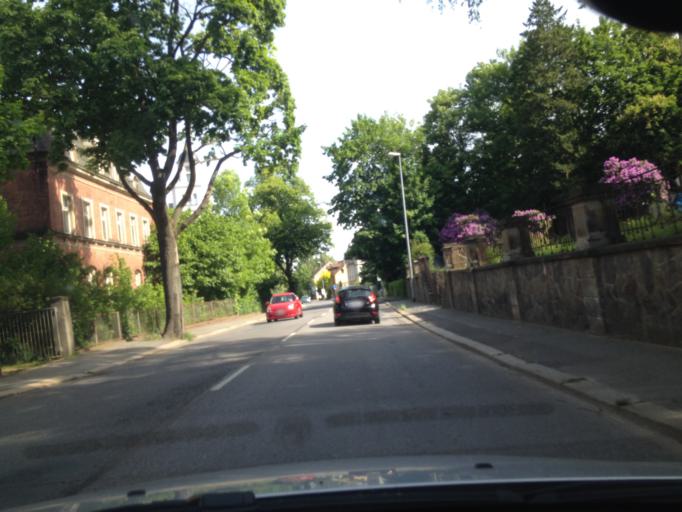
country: DE
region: Saxony
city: Burkhardtsdorf
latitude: 50.7808
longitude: 12.9251
